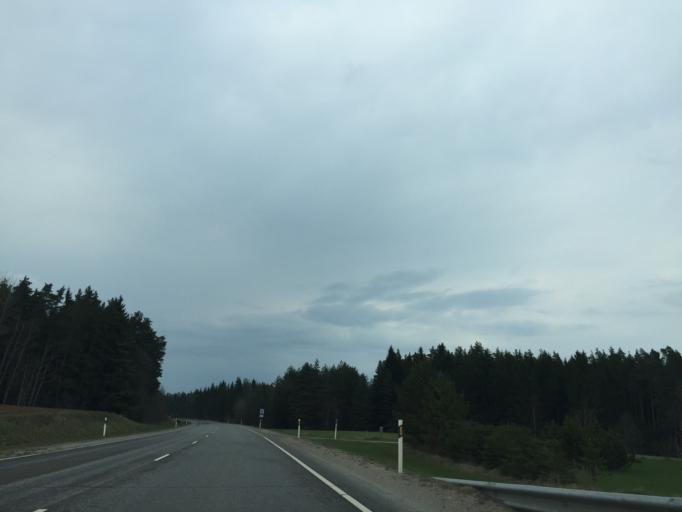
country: EE
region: Tartu
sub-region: UElenurme vald
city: Ulenurme
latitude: 58.0957
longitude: 26.7387
